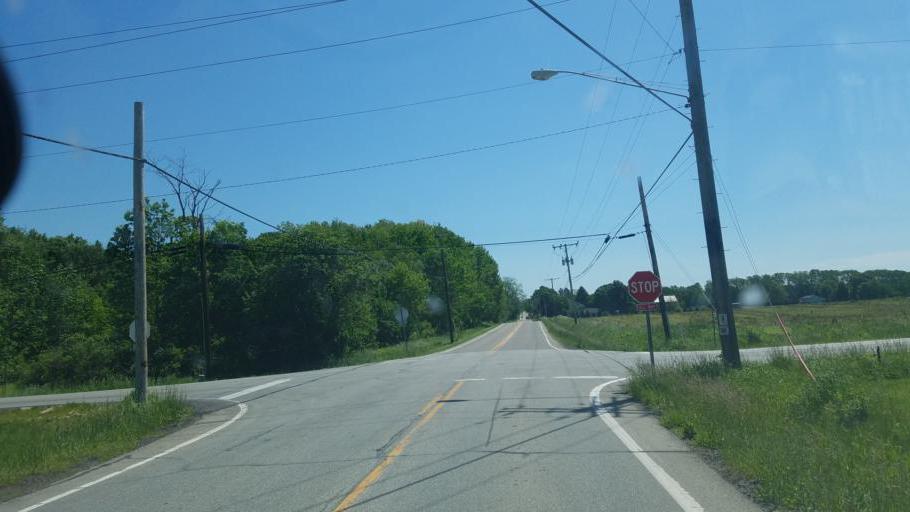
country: US
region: Ohio
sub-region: Geauga County
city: Bainbridge
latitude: 41.4329
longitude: -81.2723
